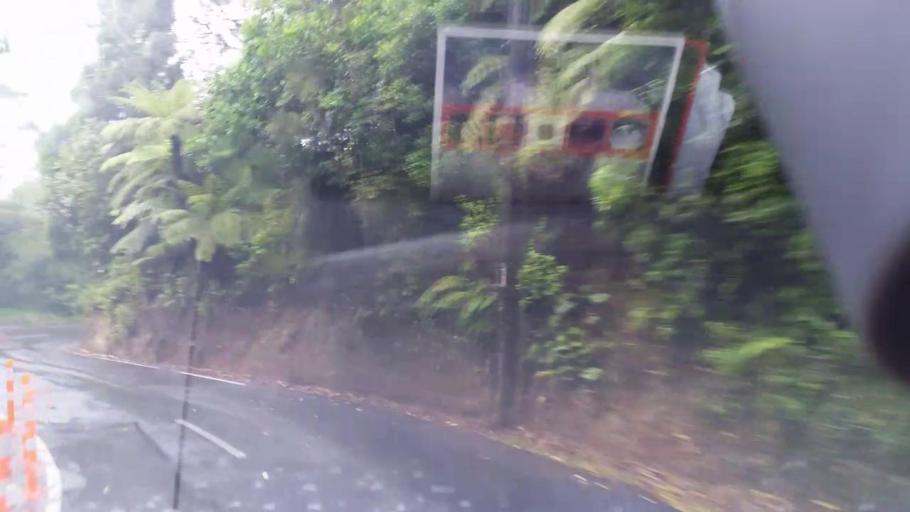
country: NZ
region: Auckland
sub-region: Auckland
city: Waitakere
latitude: -36.9104
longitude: 174.5685
